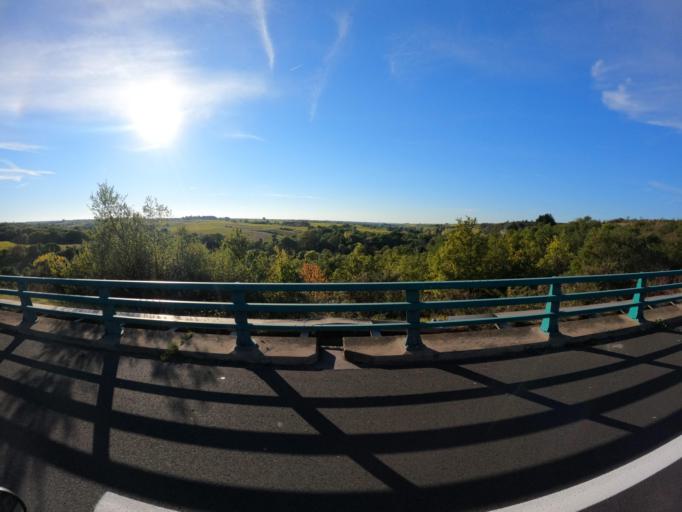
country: FR
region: Pays de la Loire
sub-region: Departement de Maine-et-Loire
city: Beaulieu-sur-Layon
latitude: 47.3120
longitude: -0.6069
